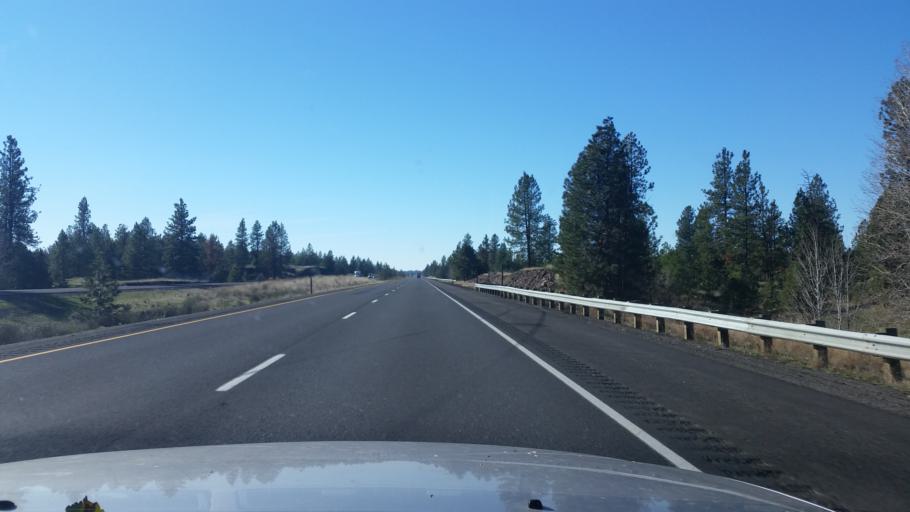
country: US
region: Washington
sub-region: Spokane County
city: Medical Lake
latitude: 47.4602
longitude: -117.7561
